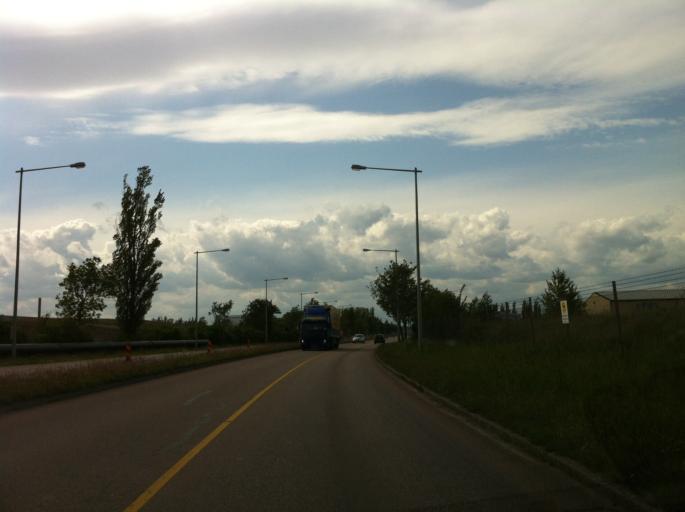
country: SE
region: Skane
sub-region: Landskrona
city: Landskrona
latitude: 55.8647
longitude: 12.8648
